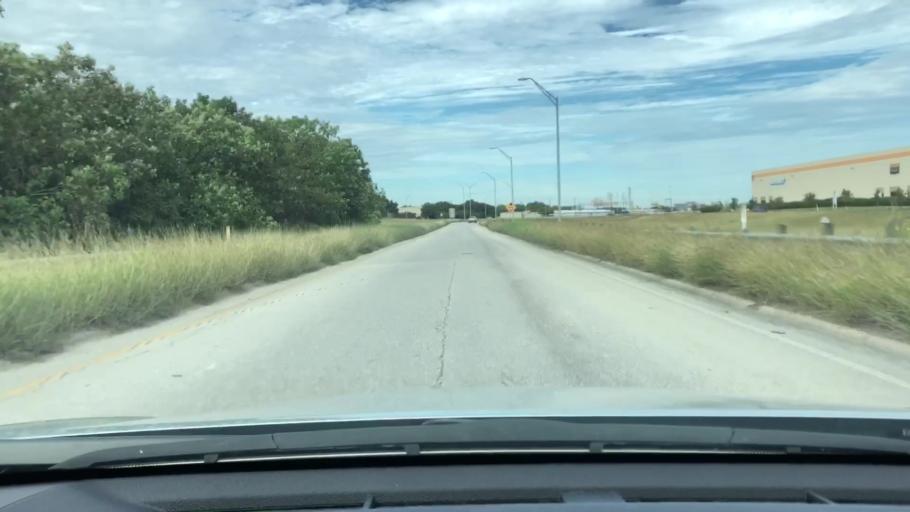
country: US
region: Texas
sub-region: Bexar County
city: Kirby
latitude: 29.4374
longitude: -98.3886
